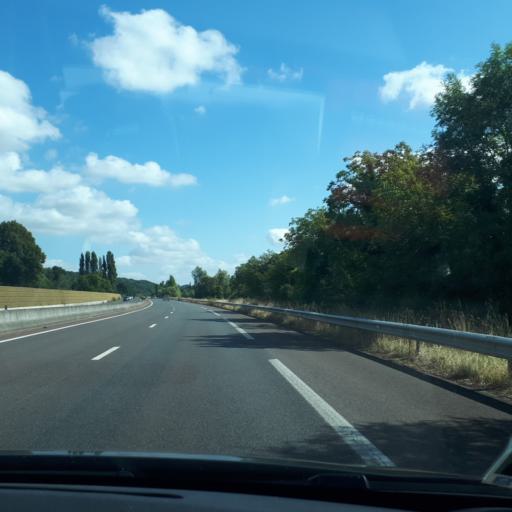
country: FR
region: Centre
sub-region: Departement du Loir-et-Cher
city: Moree
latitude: 47.8776
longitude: 1.1601
